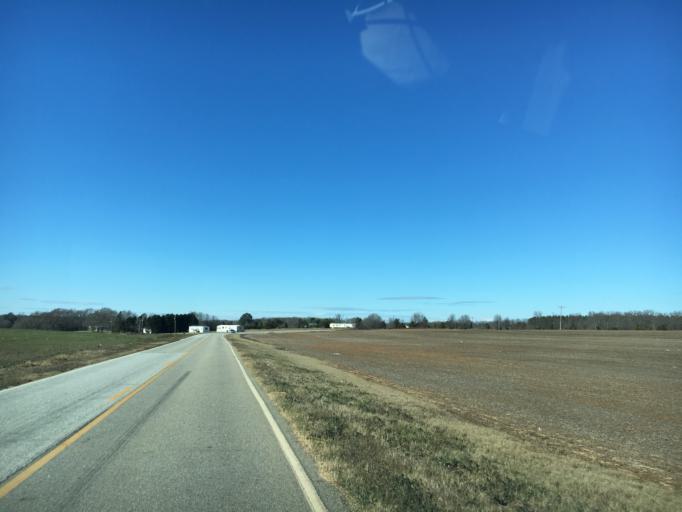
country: US
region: Georgia
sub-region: Hart County
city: Hartwell
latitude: 34.2933
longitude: -82.9826
